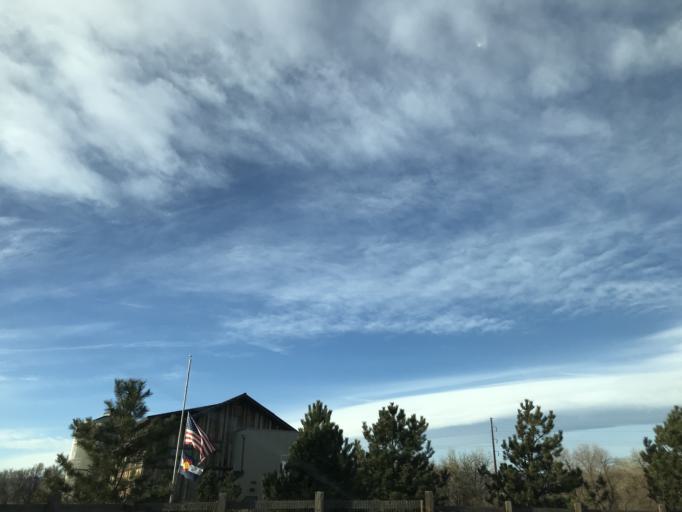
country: US
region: Colorado
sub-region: Arapahoe County
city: Columbine Valley
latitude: 39.5929
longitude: -105.0248
